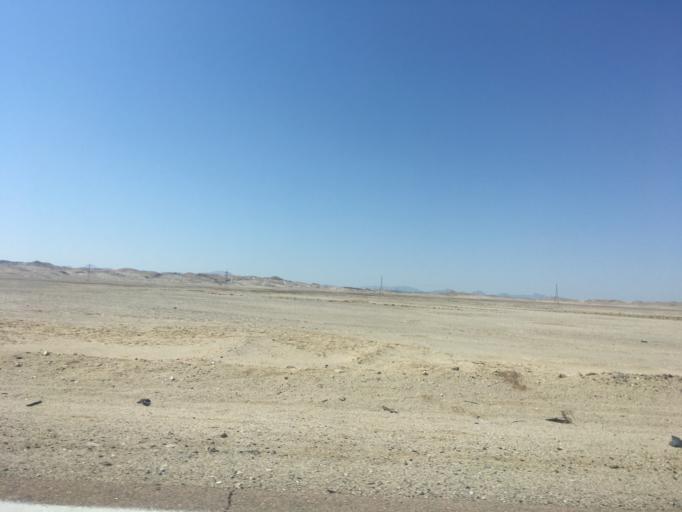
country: EG
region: Red Sea
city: Marsa Alam
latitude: 24.5002
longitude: 35.1451
